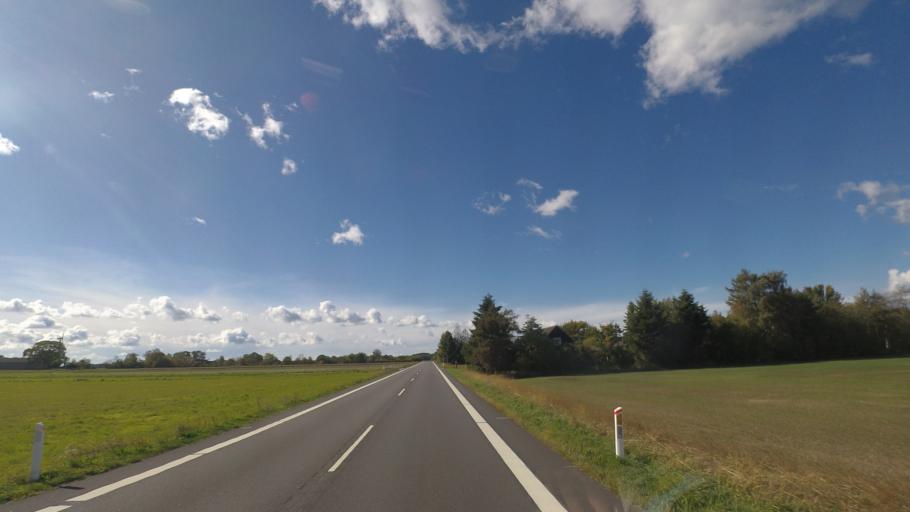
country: DK
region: Capital Region
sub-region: Bornholm Kommune
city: Nexo
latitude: 55.0609
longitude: 15.0575
